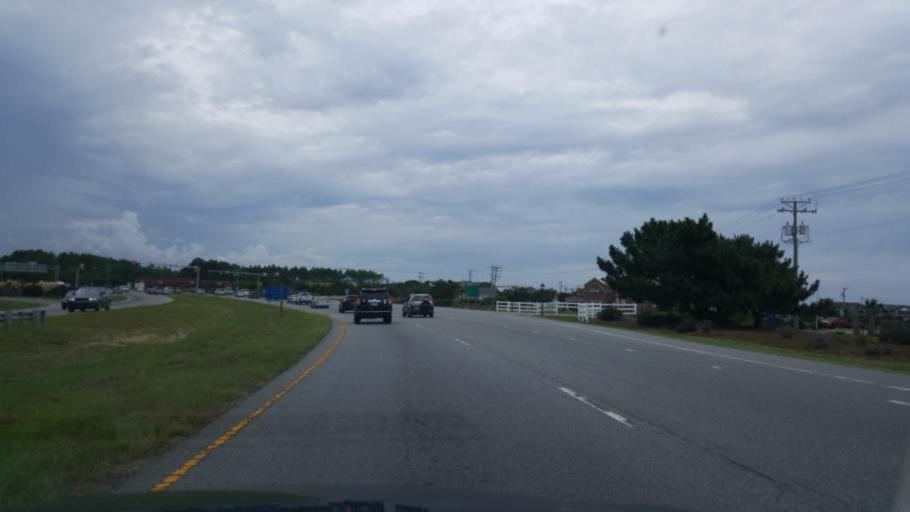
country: US
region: North Carolina
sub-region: Dare County
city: Kitty Hawk
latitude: 36.0981
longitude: -75.7130
